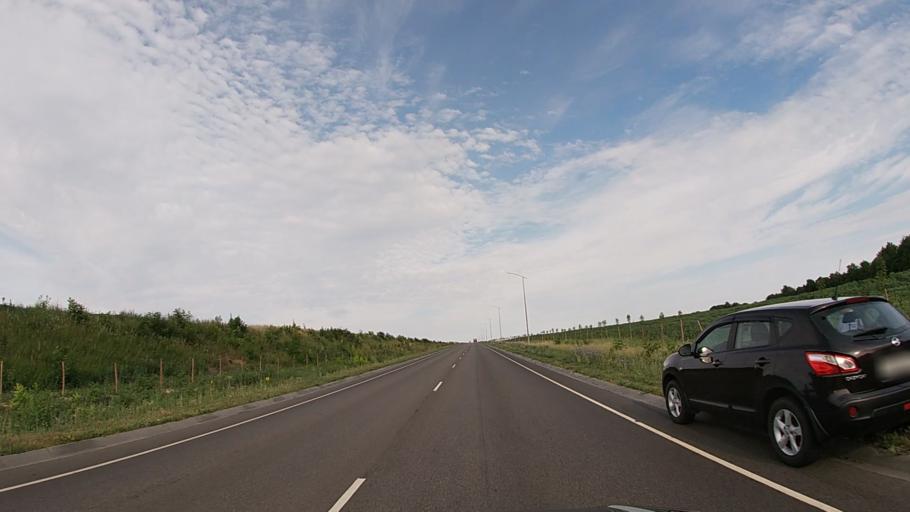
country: RU
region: Belgorod
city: Severnyy
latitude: 50.6646
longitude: 36.5166
